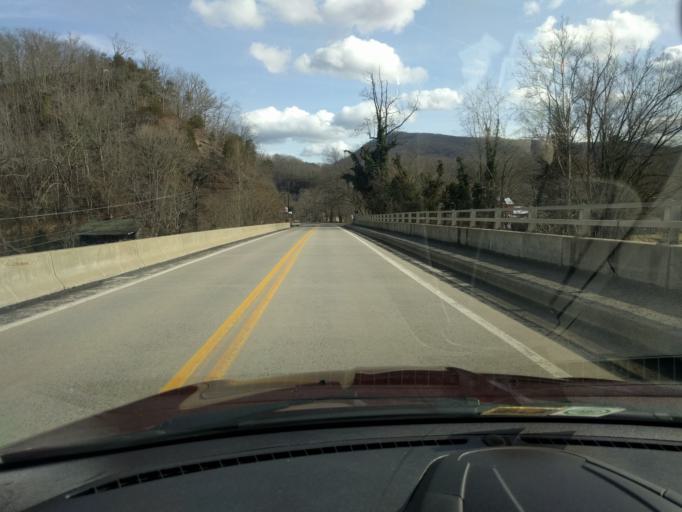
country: US
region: West Virginia
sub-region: Greenbrier County
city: Lewisburg
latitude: 37.7820
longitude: -80.3974
